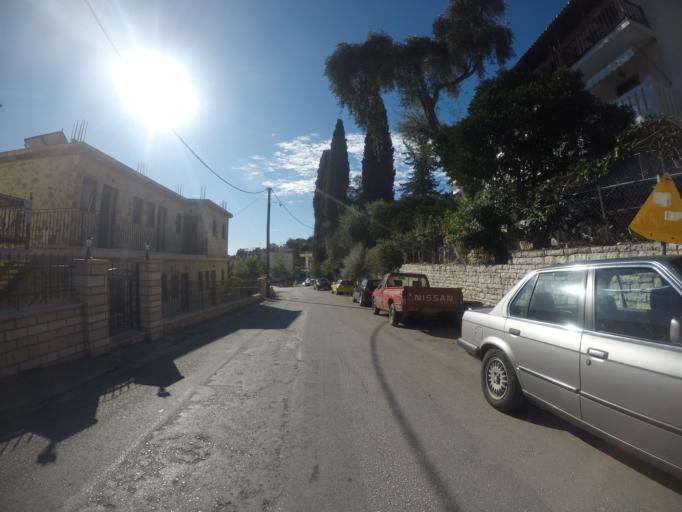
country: GR
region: Epirus
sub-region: Nomos Prevezis
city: Parga
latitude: 39.2874
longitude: 20.3973
